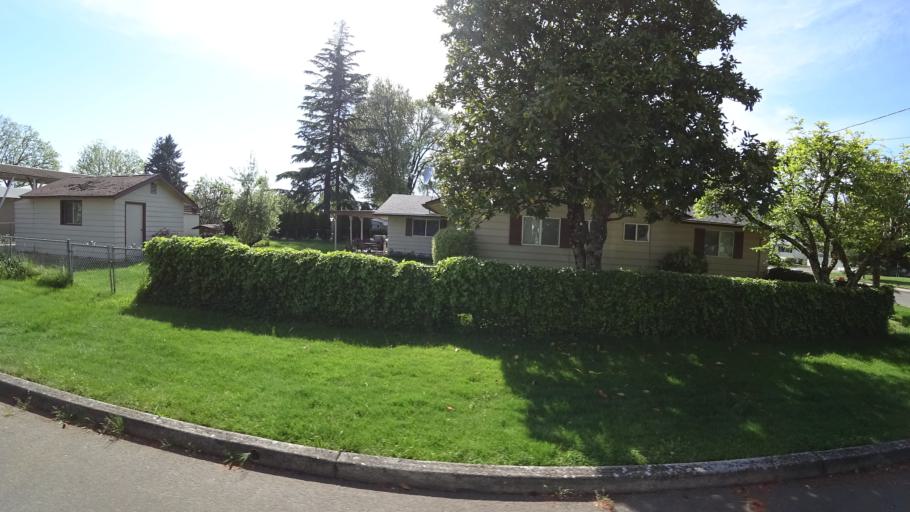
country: US
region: Oregon
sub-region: Washington County
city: Hillsboro
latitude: 45.5112
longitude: -122.9641
